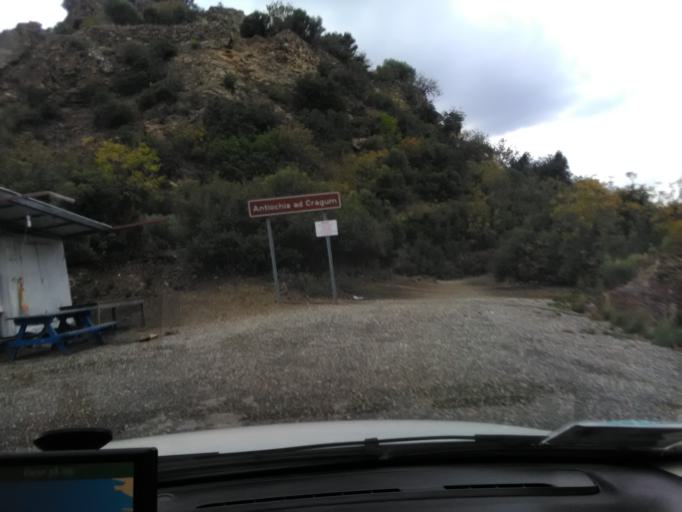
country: TR
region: Antalya
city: Gazipasa
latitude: 36.1573
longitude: 32.4162
